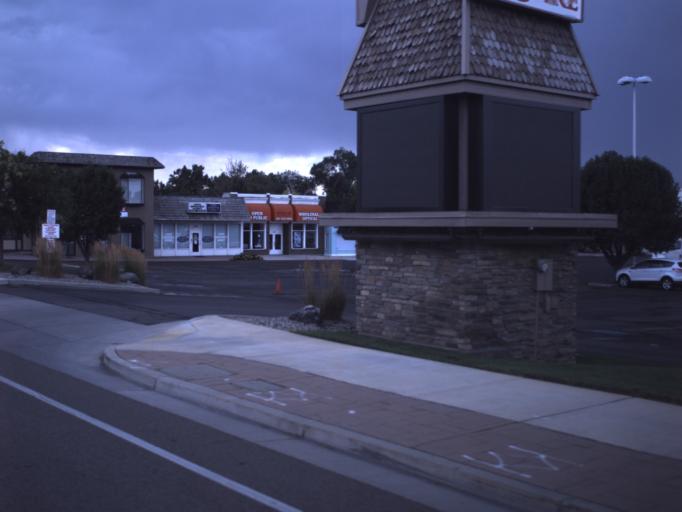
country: US
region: Utah
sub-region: Salt Lake County
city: White City
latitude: 40.5795
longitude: -111.8723
